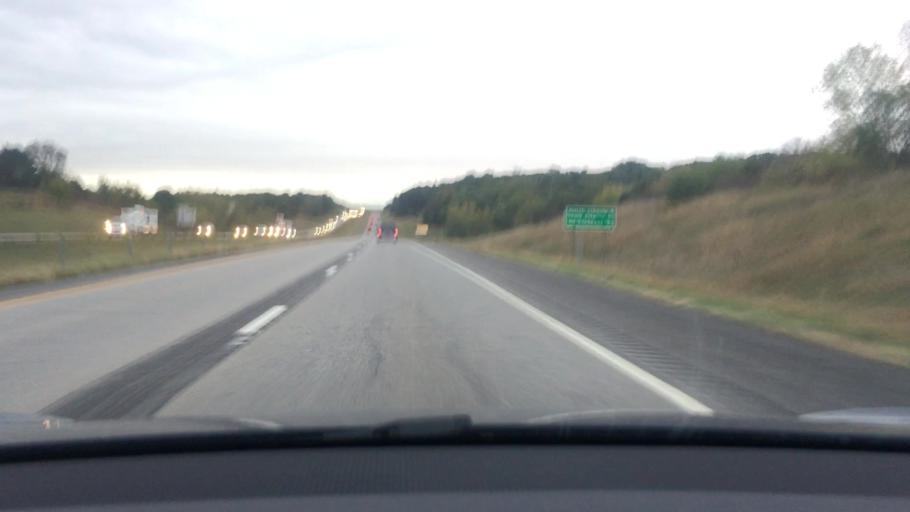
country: US
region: Iowa
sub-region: Linn County
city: Ely
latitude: 41.8317
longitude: -91.6618
